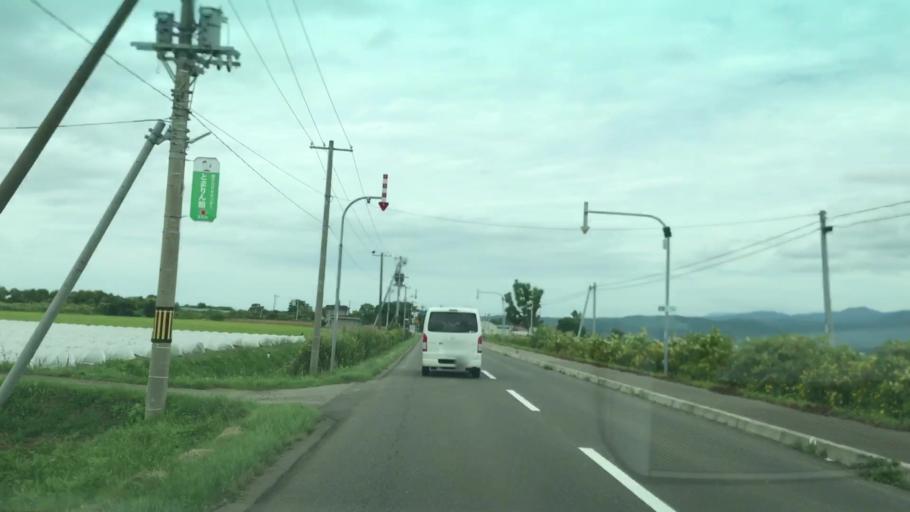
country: JP
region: Hokkaido
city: Iwanai
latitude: 43.0008
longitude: 140.5884
